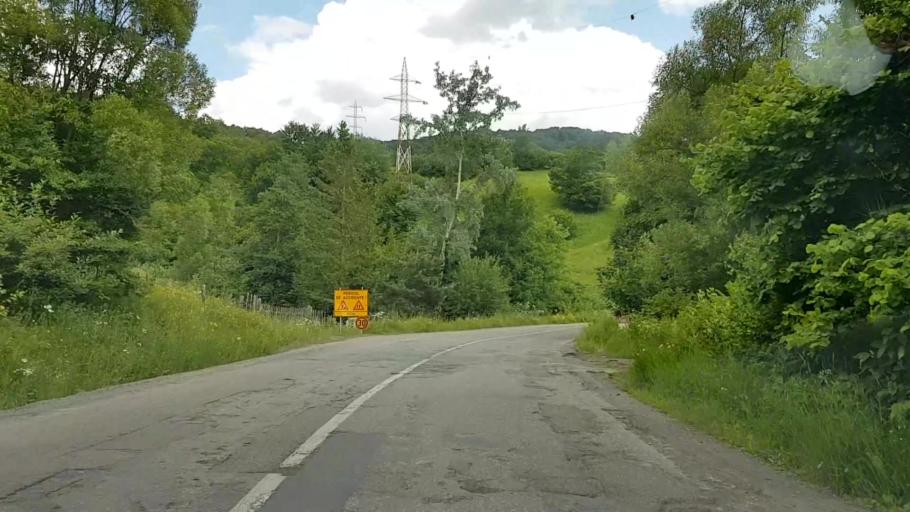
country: RO
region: Neamt
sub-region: Comuna Pangarati
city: Pangarati
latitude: 46.9400
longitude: 26.1267
